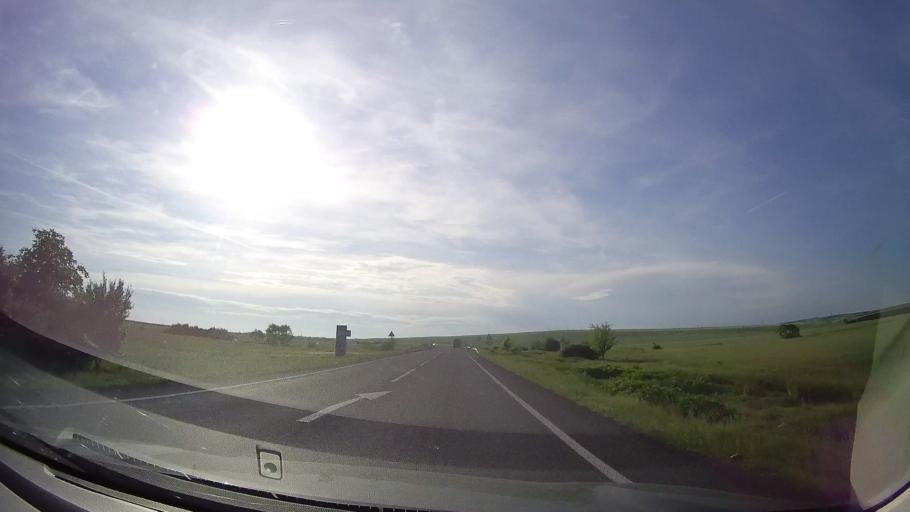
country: RO
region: Timis
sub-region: Comuna Topolovatu Mare
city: Topolovatu Mare
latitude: 45.7894
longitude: 21.5787
